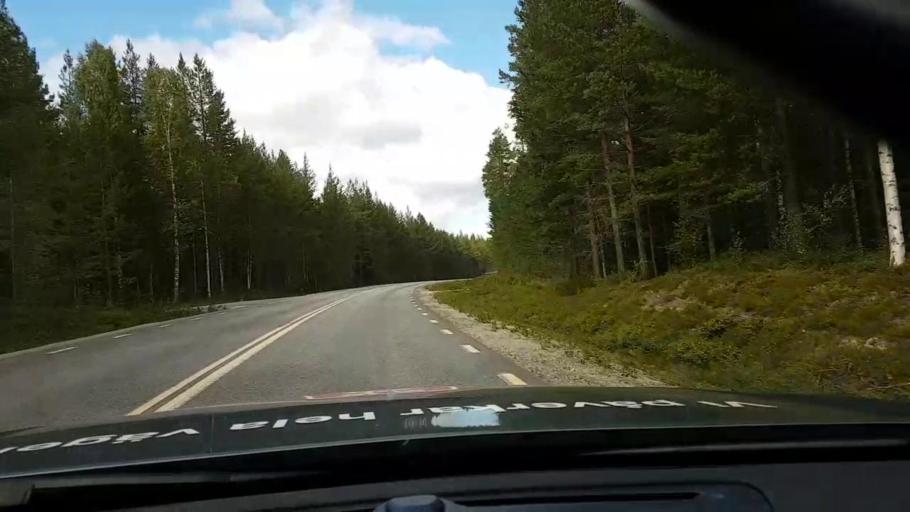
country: SE
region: Vaesternorrland
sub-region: OErnskoeldsviks Kommun
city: Bredbyn
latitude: 63.5318
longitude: 17.9687
